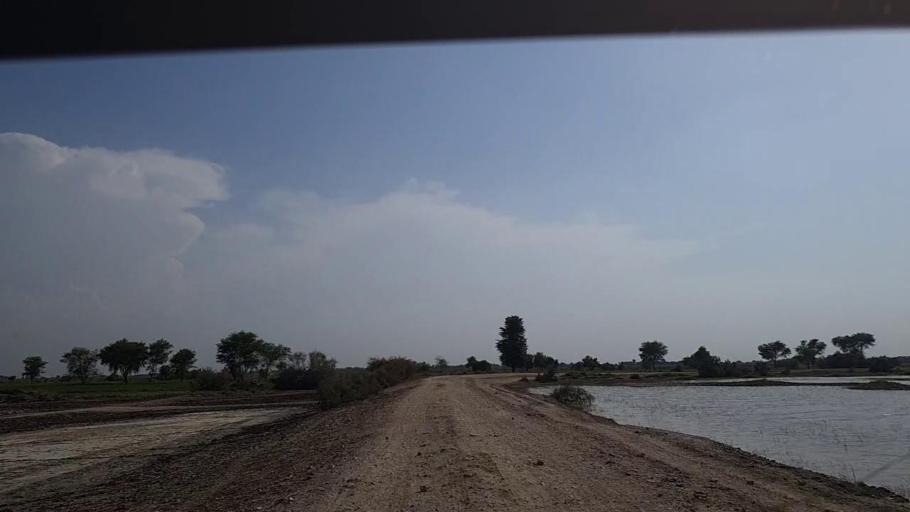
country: PK
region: Sindh
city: Khanpur
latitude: 27.8371
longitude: 69.3257
